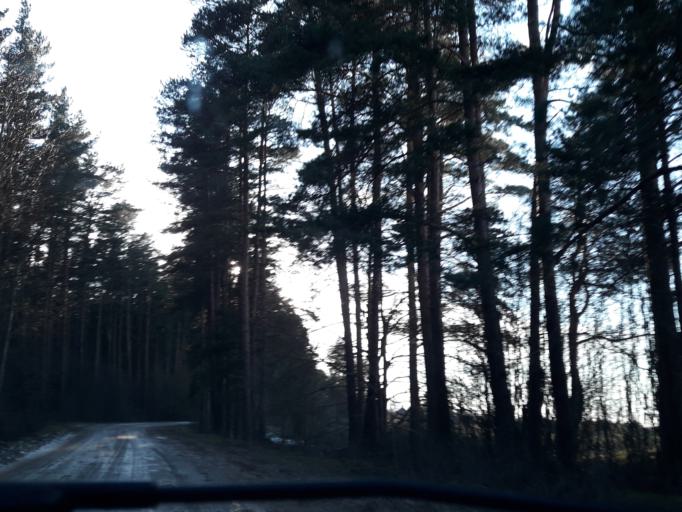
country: LV
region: Kekava
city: Kekava
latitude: 56.8735
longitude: 24.2146
